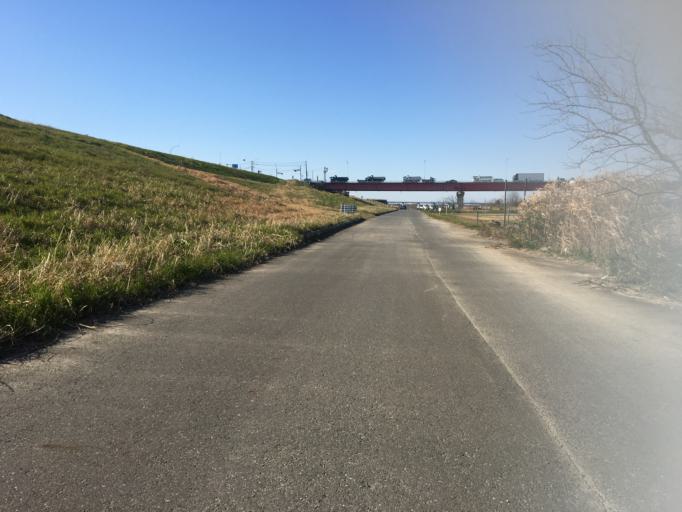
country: JP
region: Saitama
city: Shiki
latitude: 35.8329
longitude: 139.6058
